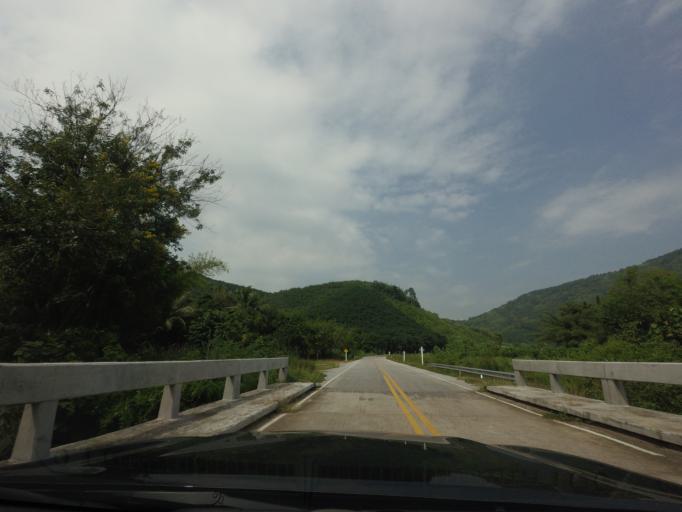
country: LA
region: Xiagnabouli
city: Muang Kenthao
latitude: 17.7735
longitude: 101.5272
